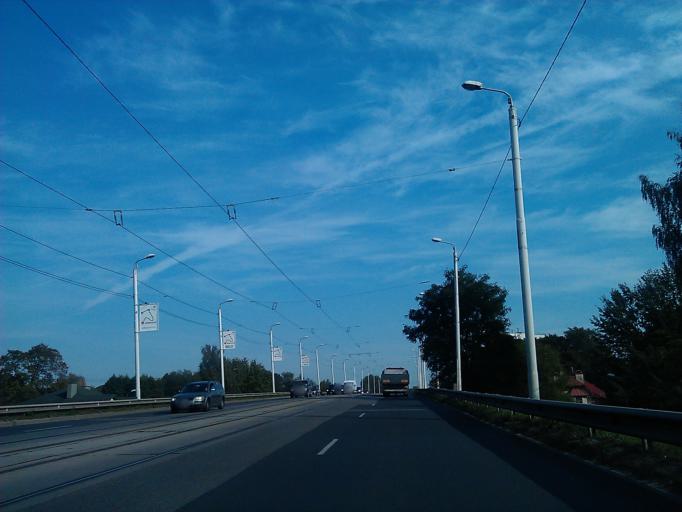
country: LV
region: Marupe
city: Marupe
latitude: 56.9519
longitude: 24.0413
